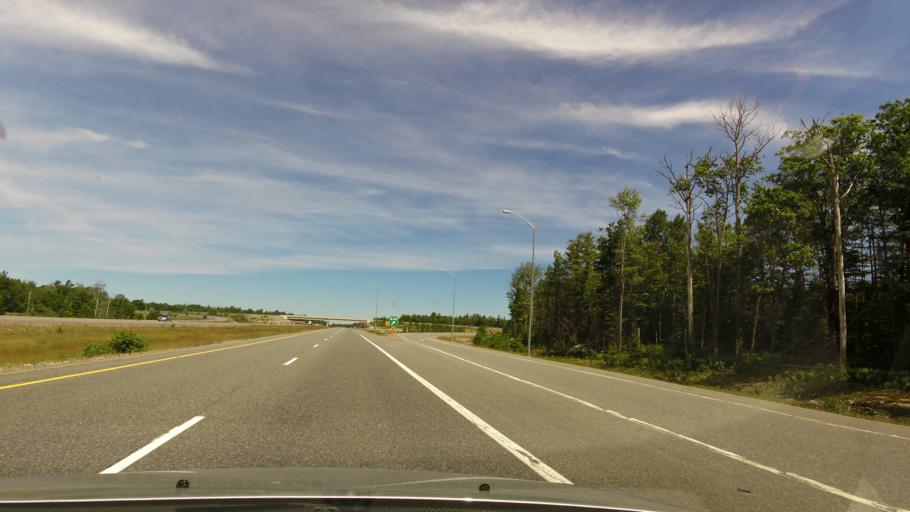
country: CA
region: Ontario
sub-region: Parry Sound District
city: Parry Sound
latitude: 45.4177
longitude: -80.0693
